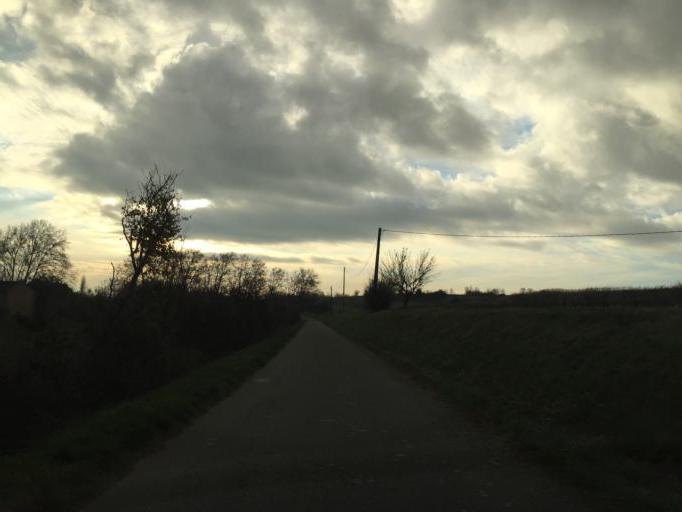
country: FR
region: Provence-Alpes-Cote d'Azur
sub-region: Departement du Vaucluse
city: Courthezon
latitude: 44.1041
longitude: 4.8793
